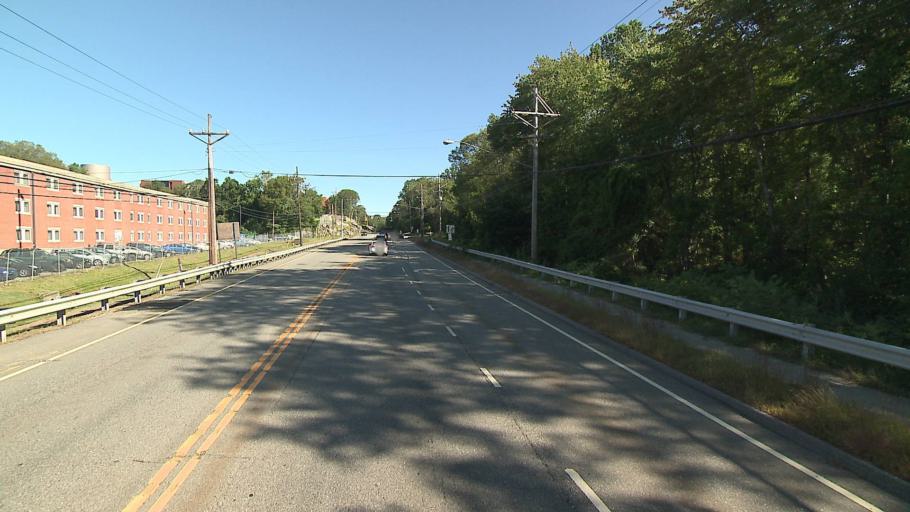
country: US
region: Connecticut
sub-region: New London County
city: Conning Towers-Nautilus Park
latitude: 41.3939
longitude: -72.0806
